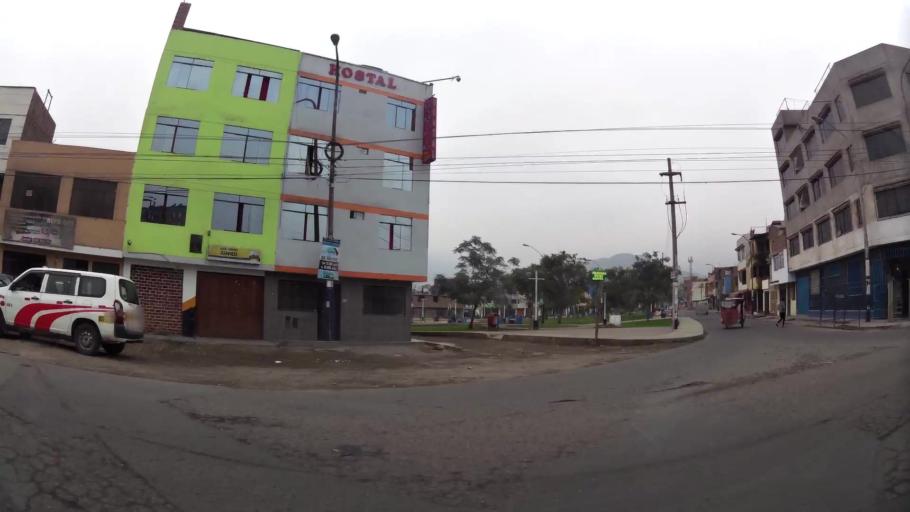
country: PE
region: Lima
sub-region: Lima
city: Independencia
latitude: -11.9540
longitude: -76.9833
